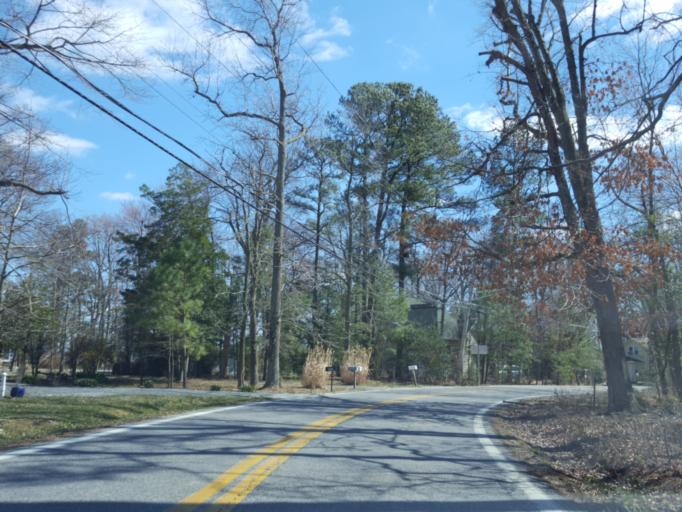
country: US
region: Maryland
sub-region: Calvert County
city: North Beach
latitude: 38.7270
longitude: -76.5288
